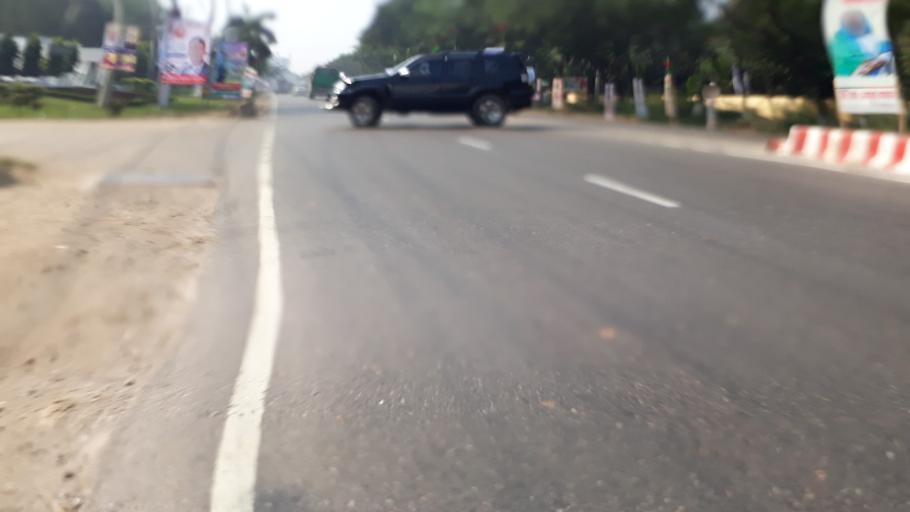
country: BD
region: Dhaka
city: Tungi
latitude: 23.8643
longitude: 90.2689
